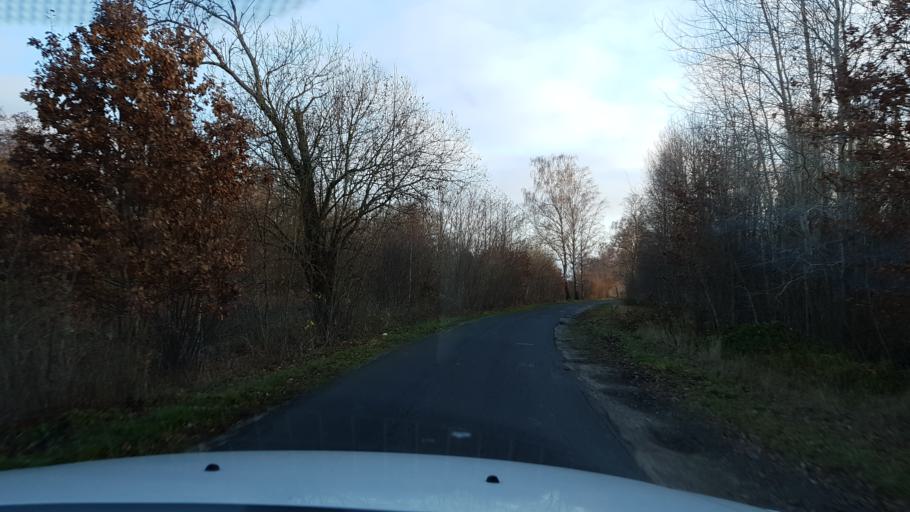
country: PL
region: West Pomeranian Voivodeship
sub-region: Koszalin
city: Koszalin
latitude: 54.1087
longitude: 16.1243
